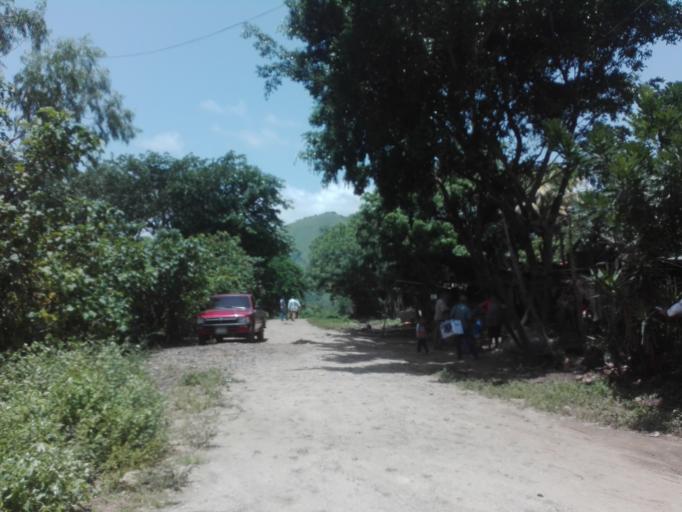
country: GT
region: Escuintla
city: Guanagazapa
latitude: 14.2852
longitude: -90.5646
